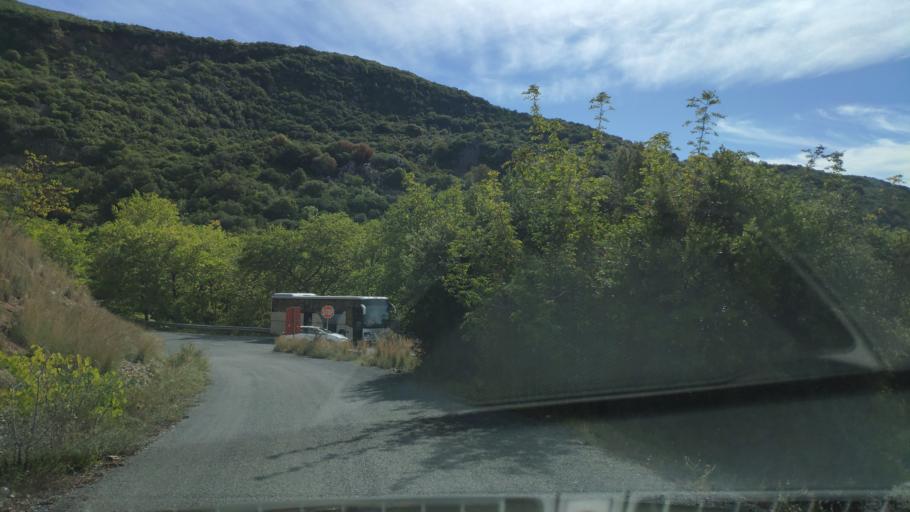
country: GR
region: Peloponnese
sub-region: Nomos Arkadias
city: Dimitsana
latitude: 37.5345
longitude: 22.0520
